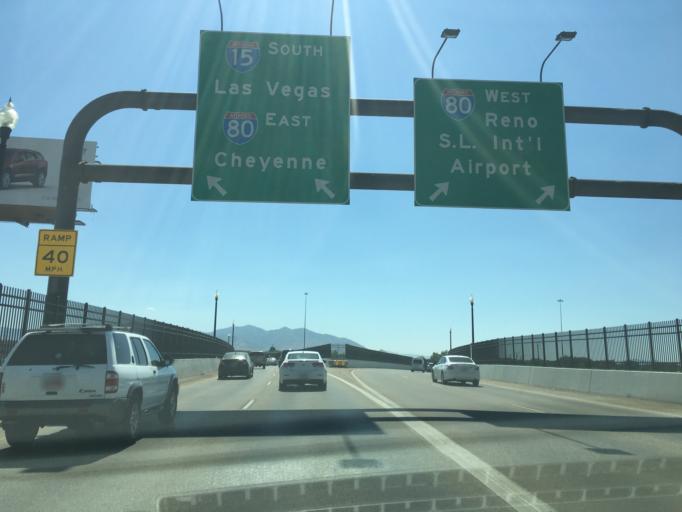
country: US
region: Utah
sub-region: Salt Lake County
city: Salt Lake City
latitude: 40.7582
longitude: -111.9093
